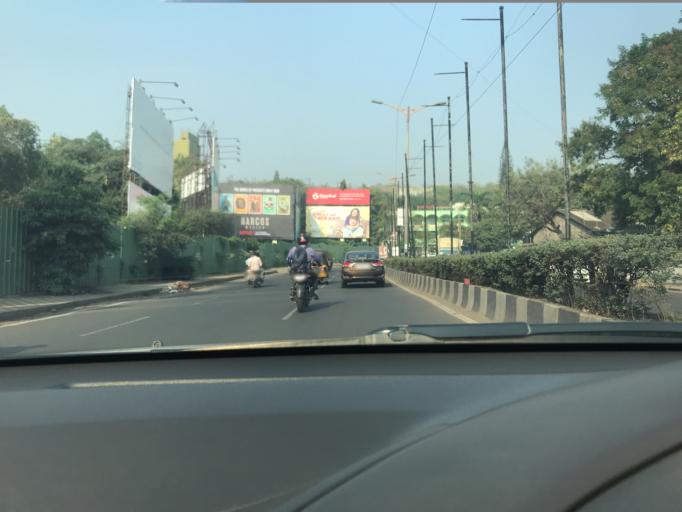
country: IN
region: Maharashtra
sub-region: Pune Division
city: Shivaji Nagar
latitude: 18.5202
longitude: 73.8300
